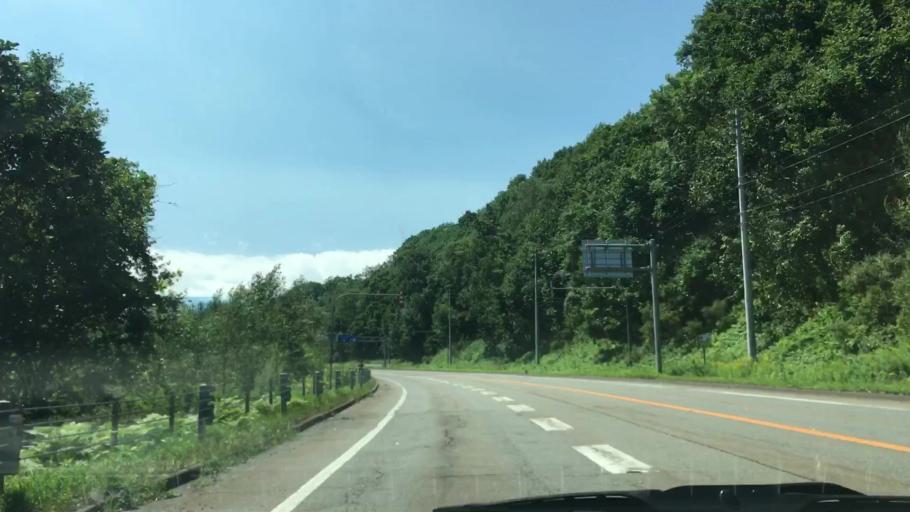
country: JP
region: Hokkaido
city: Otofuke
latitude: 43.2378
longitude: 143.5313
